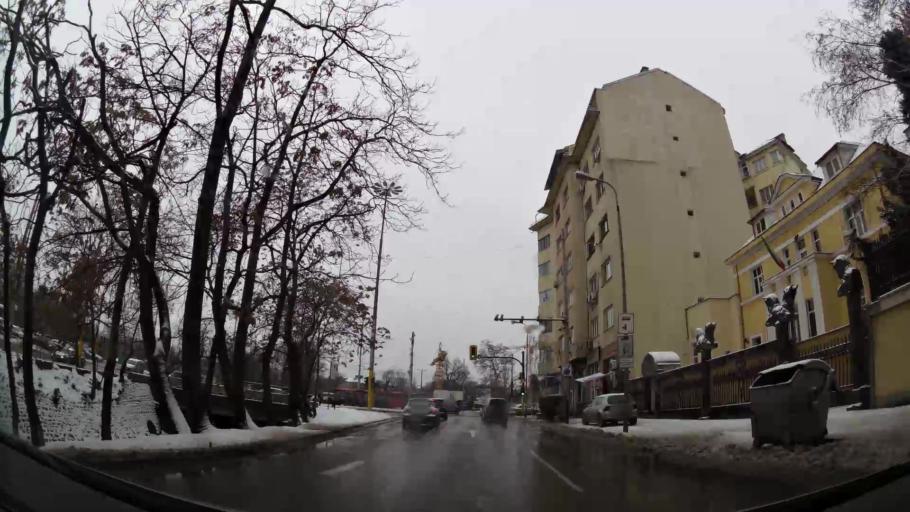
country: BG
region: Sofia-Capital
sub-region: Stolichna Obshtina
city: Sofia
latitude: 42.6909
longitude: 23.3380
